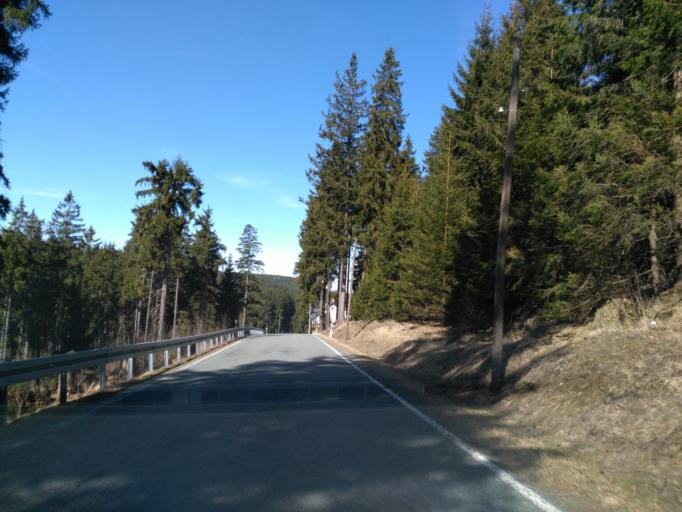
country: DE
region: Saxony
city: Kurort Oberwiesenthal
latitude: 50.4389
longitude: 12.8831
